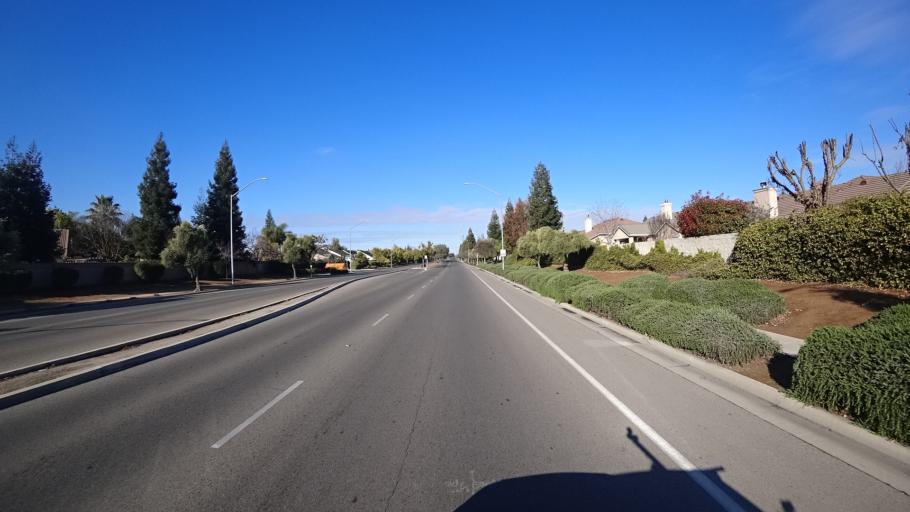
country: US
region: California
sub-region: Fresno County
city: West Park
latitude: 36.8222
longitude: -119.8754
